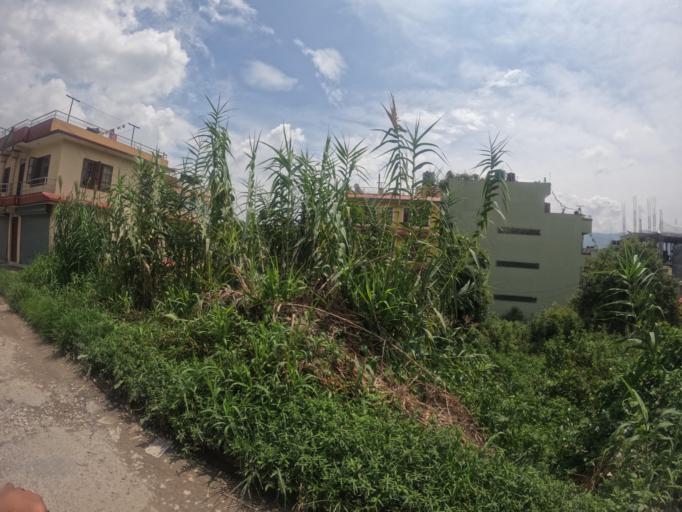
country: NP
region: Central Region
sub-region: Bagmati Zone
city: Bhaktapur
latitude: 27.6763
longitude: 85.3807
